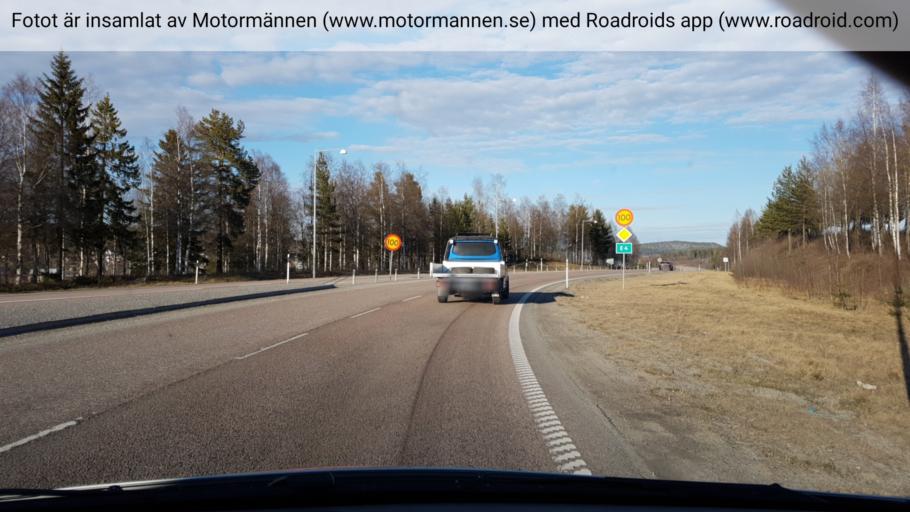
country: SE
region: Vaesternorrland
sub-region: OErnskoeldsviks Kommun
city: Ornskoldsvik
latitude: 63.3035
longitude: 18.7355
